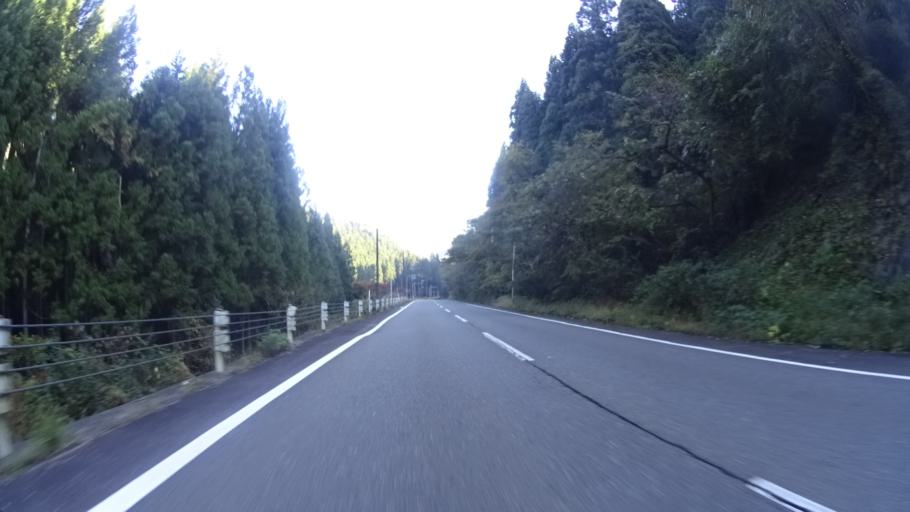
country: JP
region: Fukui
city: Maruoka
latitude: 36.1478
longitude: 136.3277
